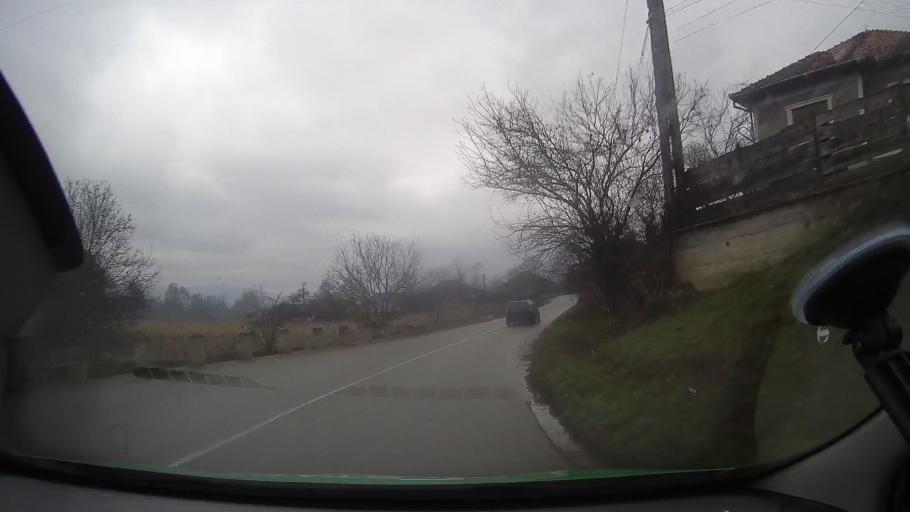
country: RO
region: Hunedoara
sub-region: Comuna Tomesti
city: Tomesti
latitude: 46.1978
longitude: 22.6468
